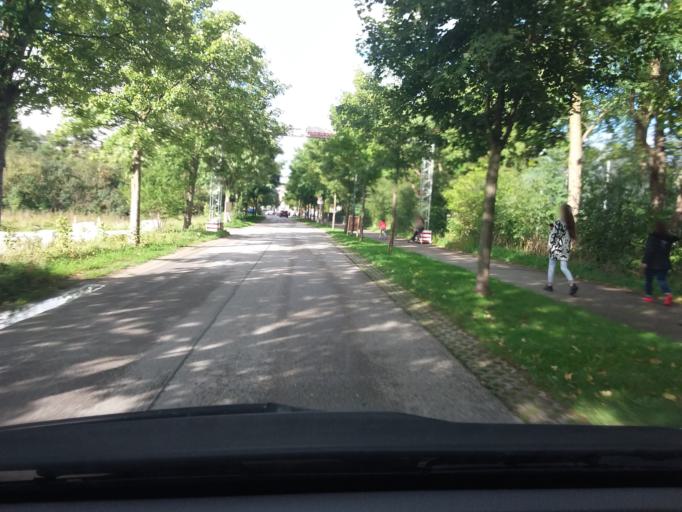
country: DE
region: Bavaria
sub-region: Upper Bavaria
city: Garching bei Munchen
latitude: 48.2486
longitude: 11.6458
